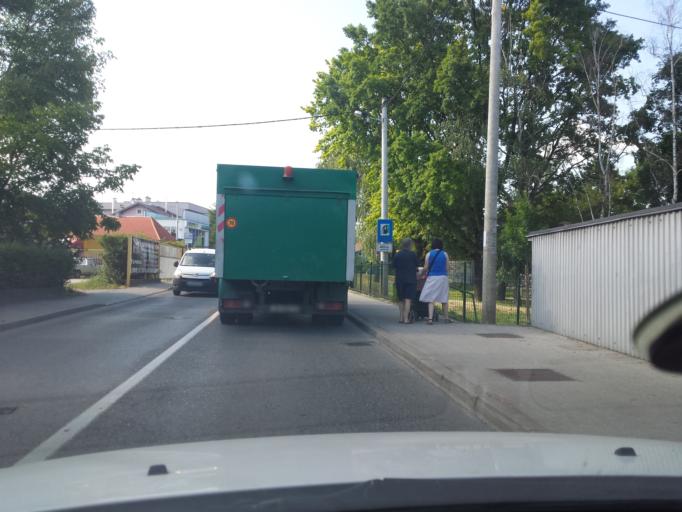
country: HR
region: Grad Zagreb
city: Jankomir
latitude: 45.8080
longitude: 15.9080
